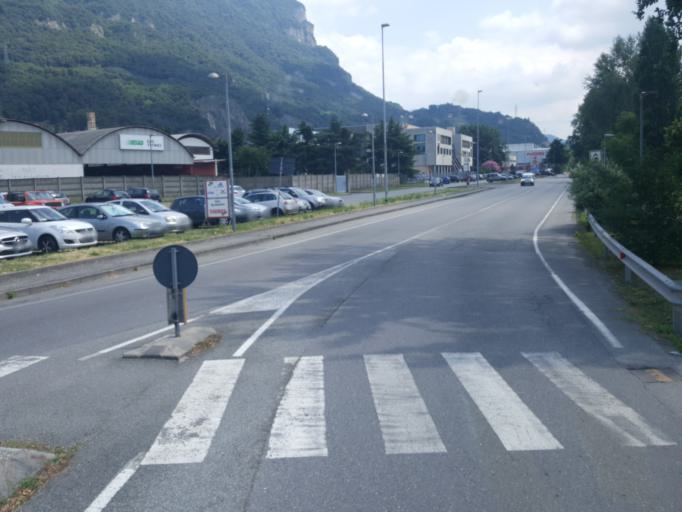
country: IT
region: Lombardy
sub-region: Provincia di Lecco
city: Pescate
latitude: 45.8296
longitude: 9.4092
